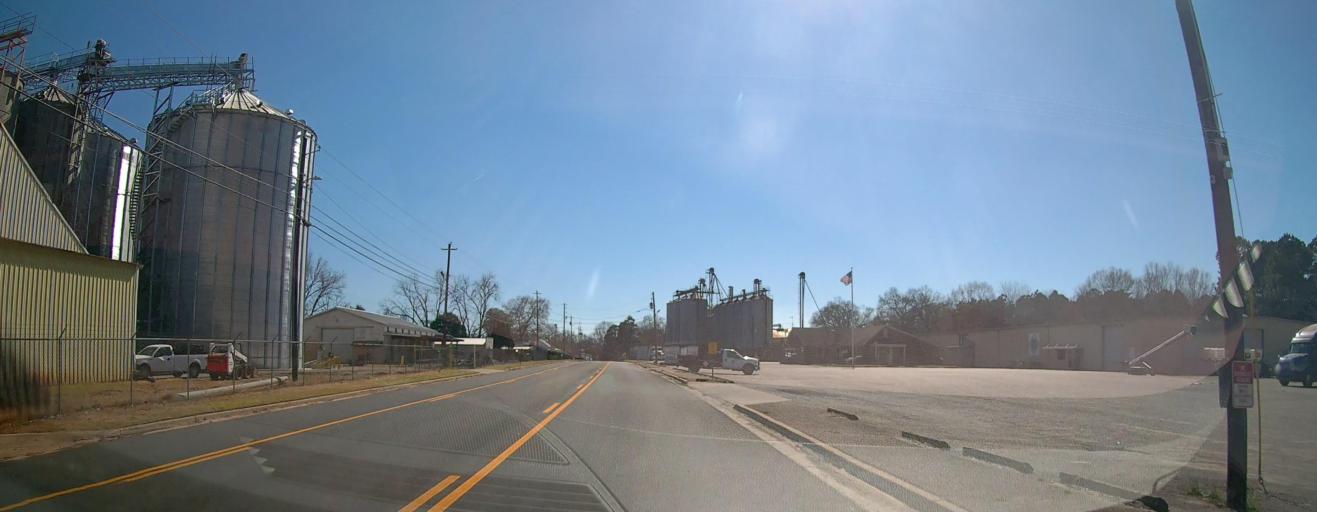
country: US
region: Georgia
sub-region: Macon County
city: Marshallville
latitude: 32.4604
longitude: -83.9406
